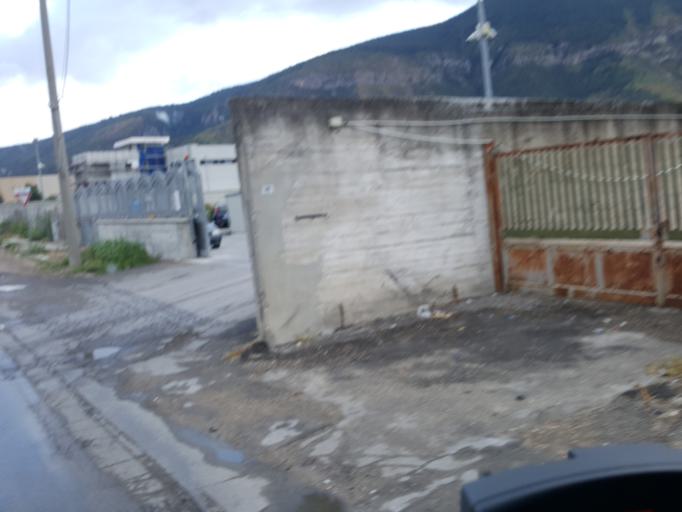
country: IT
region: Campania
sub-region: Provincia di Salerno
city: Sarno
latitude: 40.8192
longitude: 14.6025
